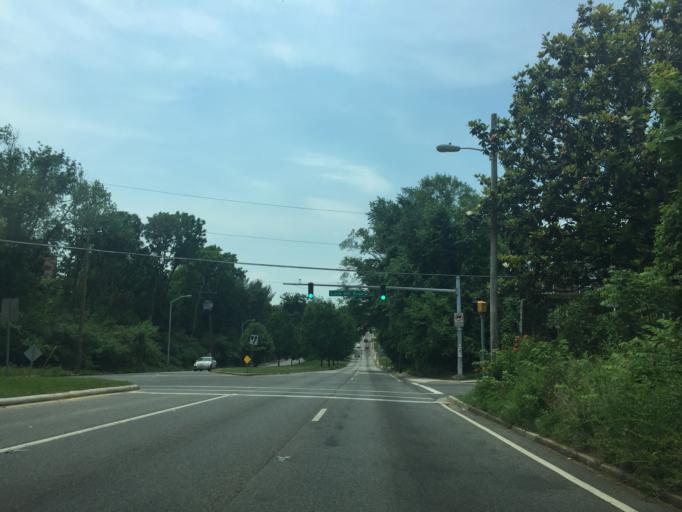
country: US
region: Maryland
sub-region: Baltimore County
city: Towson
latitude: 39.3727
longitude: -76.5819
